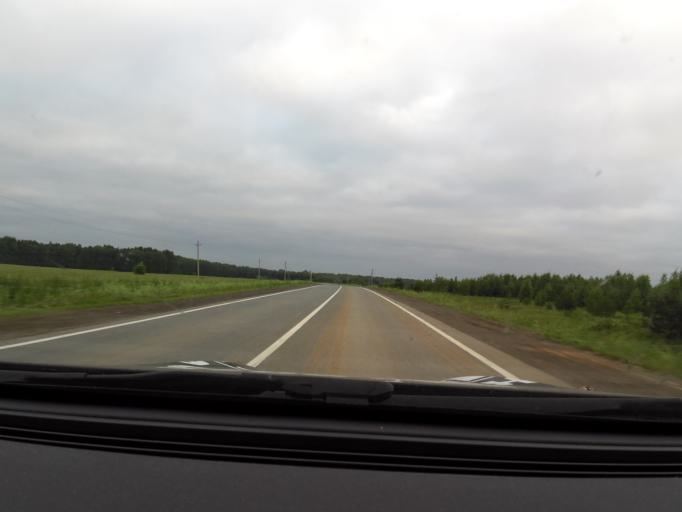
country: RU
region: Perm
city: Karagay
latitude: 58.2881
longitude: 54.8143
